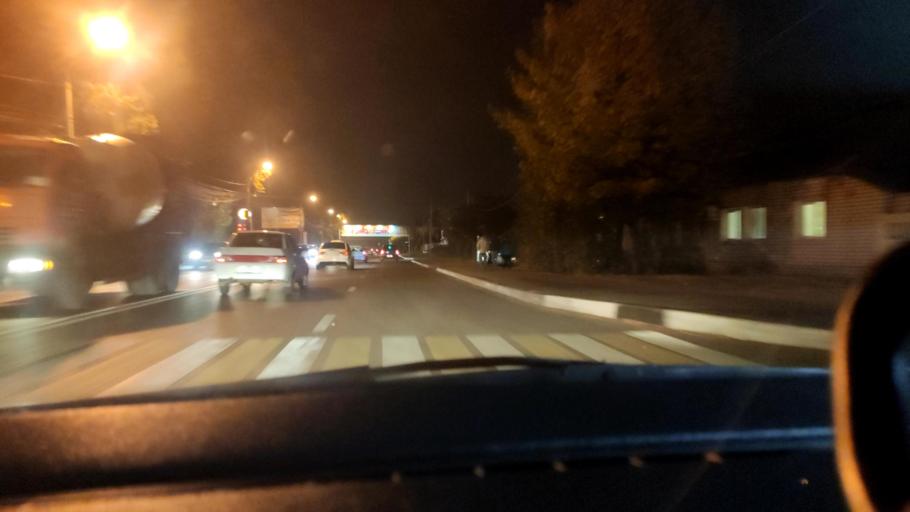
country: RU
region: Voronezj
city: Voronezh
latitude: 51.6987
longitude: 39.1964
